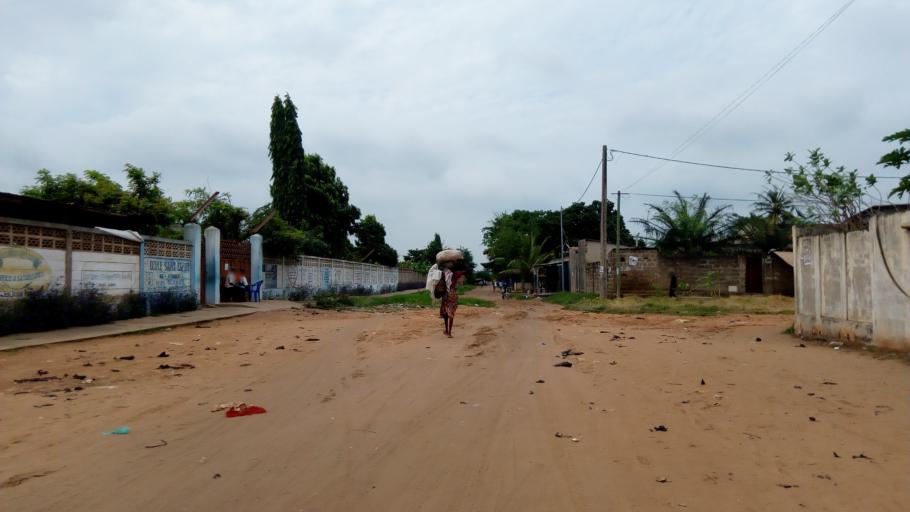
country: TG
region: Maritime
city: Lome
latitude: 6.1661
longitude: 1.2077
